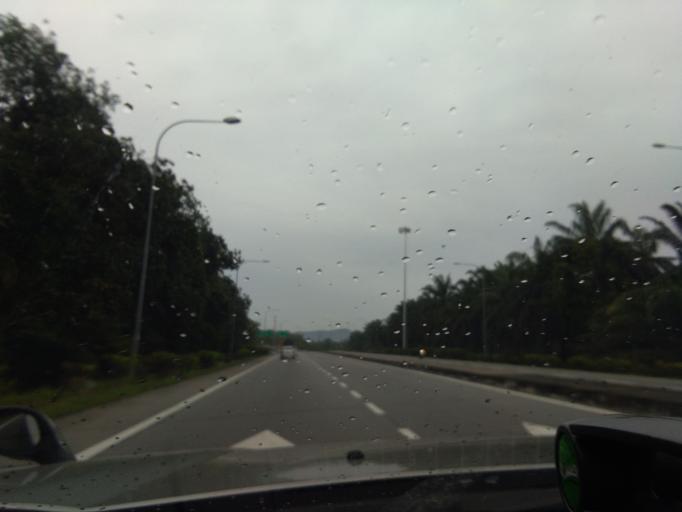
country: MY
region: Penang
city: Nibong Tebal
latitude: 5.1868
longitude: 100.4921
